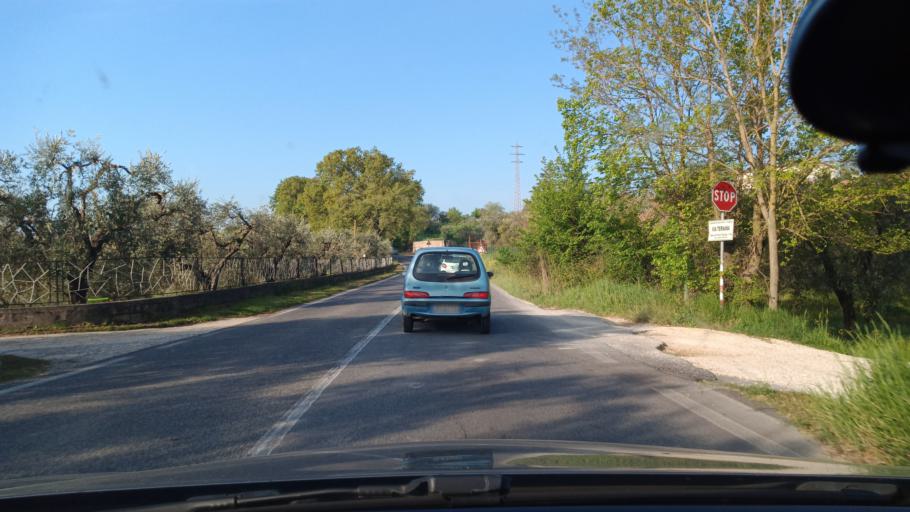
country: IT
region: Latium
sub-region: Citta metropolitana di Roma Capitale
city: Fiano Romano
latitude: 42.1856
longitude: 12.6384
